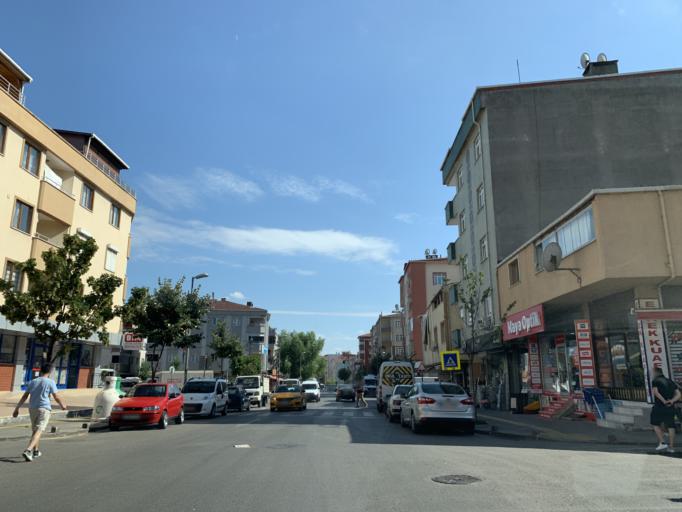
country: TR
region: Istanbul
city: Pendik
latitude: 40.8853
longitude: 29.2727
